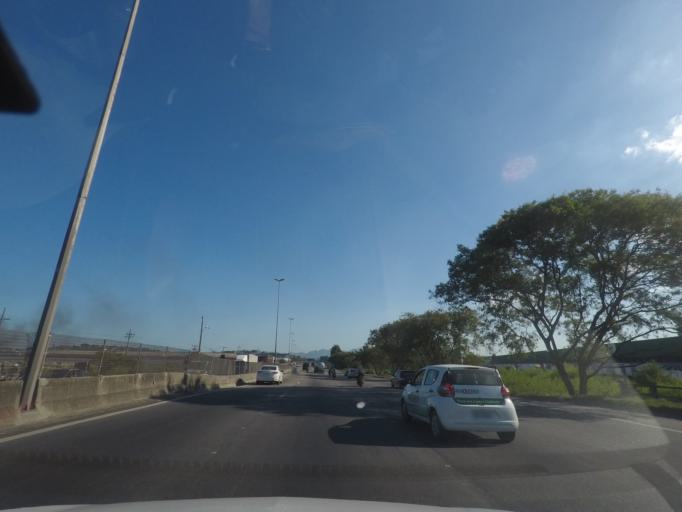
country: BR
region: Rio de Janeiro
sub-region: Duque De Caxias
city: Duque de Caxias
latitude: -22.7466
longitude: -43.2880
